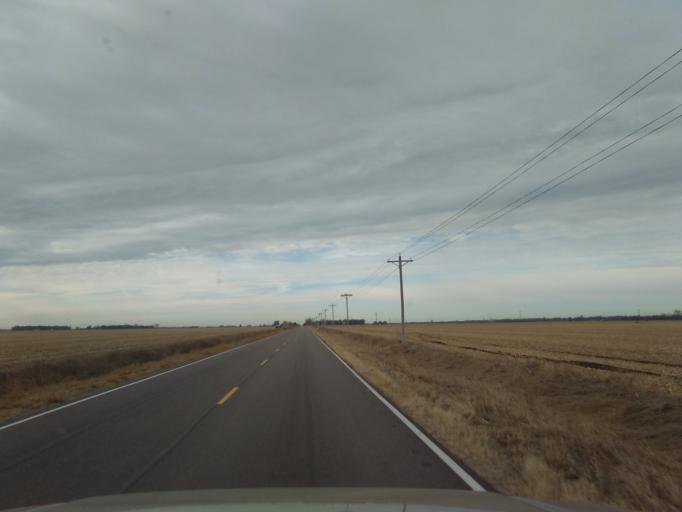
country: US
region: Nebraska
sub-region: Buffalo County
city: Gibbon
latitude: 40.6410
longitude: -98.9377
